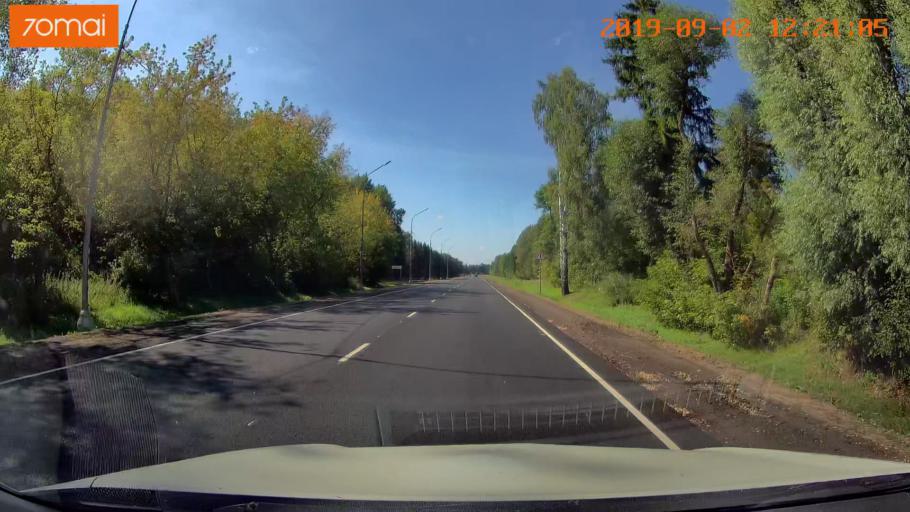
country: RU
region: Smolensk
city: Oster
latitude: 53.8897
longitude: 32.6624
